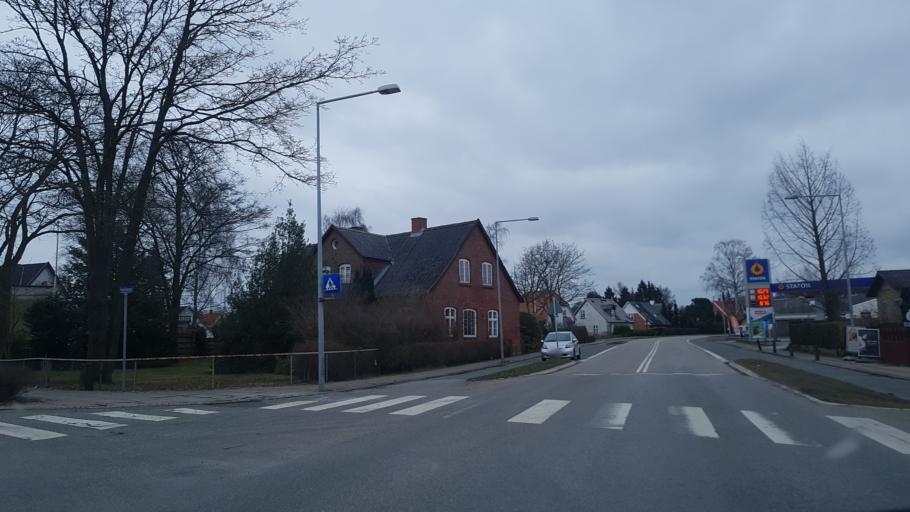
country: DK
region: Zealand
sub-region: Soro Kommune
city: Frederiksberg
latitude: 55.4168
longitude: 11.5672
